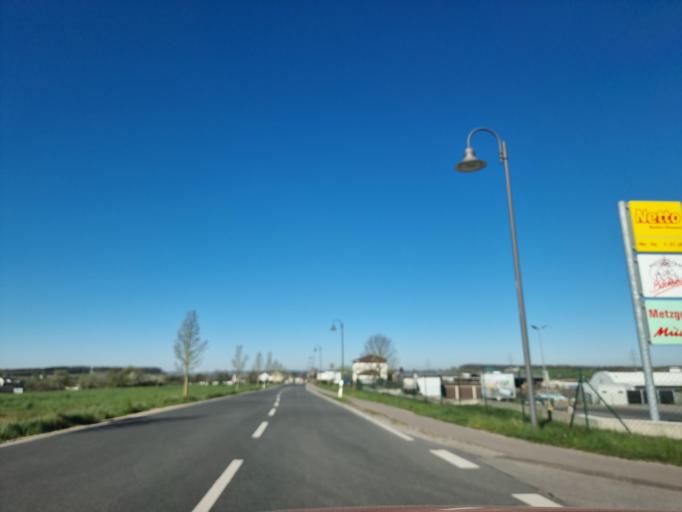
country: DE
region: Rheinland-Pfalz
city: Zemmer
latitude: 49.8973
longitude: 6.7047
